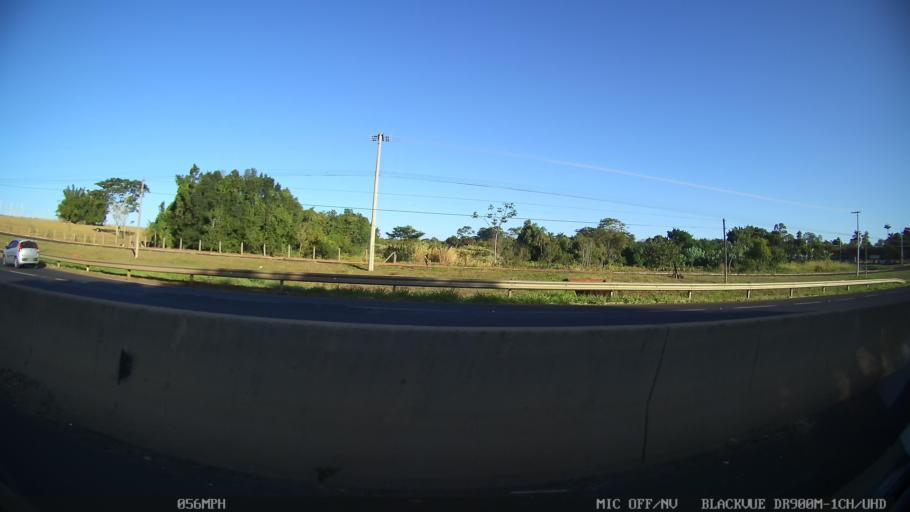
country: BR
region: Sao Paulo
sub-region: Guapiacu
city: Guapiacu
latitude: -20.7841
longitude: -49.2705
